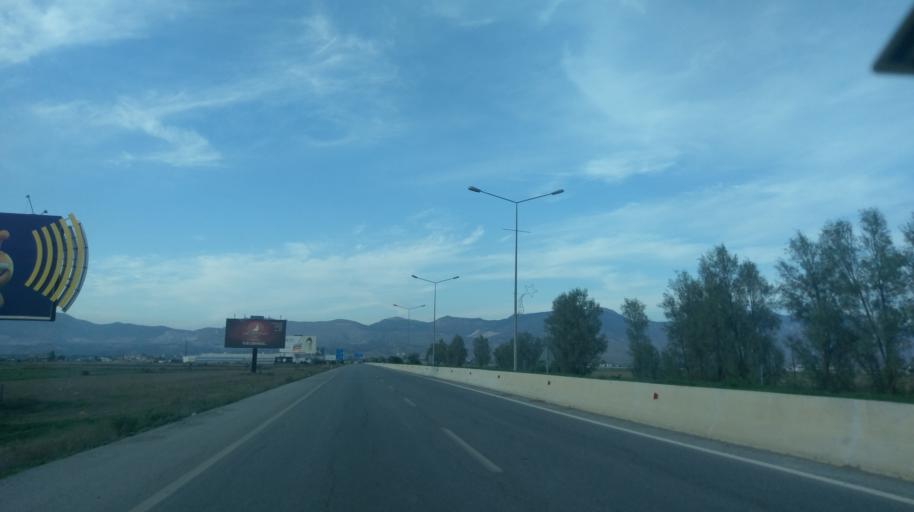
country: CY
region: Lefkosia
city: Geri
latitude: 35.2104
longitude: 33.4984
